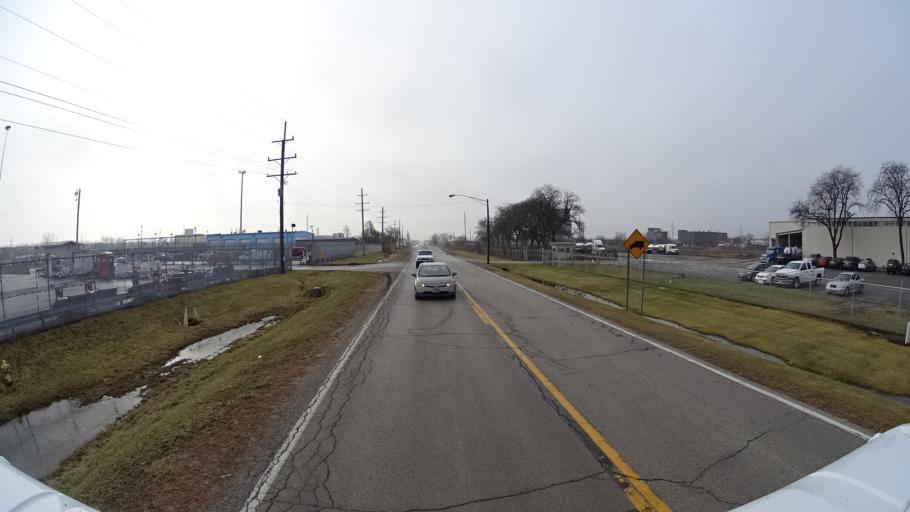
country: US
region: Illinois
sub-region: Cook County
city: Glenwood
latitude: 41.5266
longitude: -87.6165
